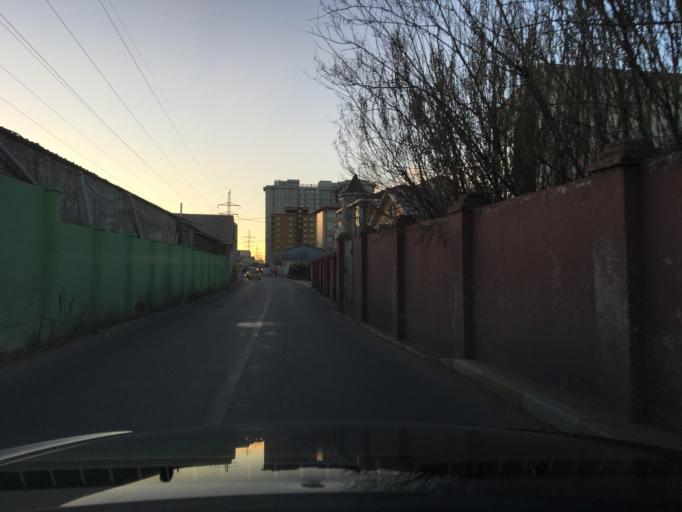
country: MN
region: Ulaanbaatar
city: Ulaanbaatar
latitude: 47.8926
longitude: 106.9115
